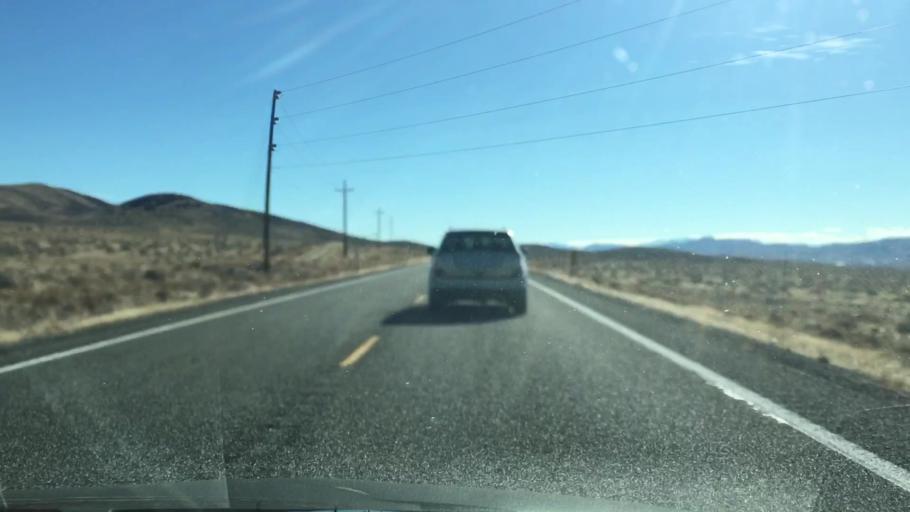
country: US
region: Nevada
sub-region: Lyon County
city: Yerington
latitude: 39.1970
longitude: -119.2128
